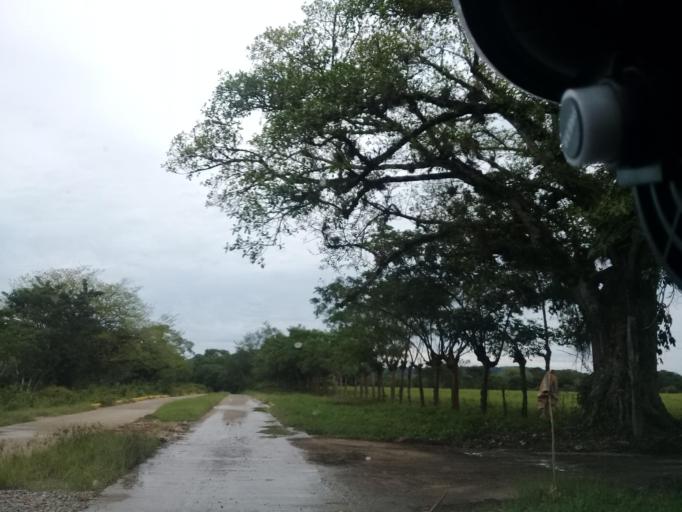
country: MX
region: Hidalgo
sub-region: Huejutla de Reyes
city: Chalahuiyapa
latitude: 21.1621
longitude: -98.3616
